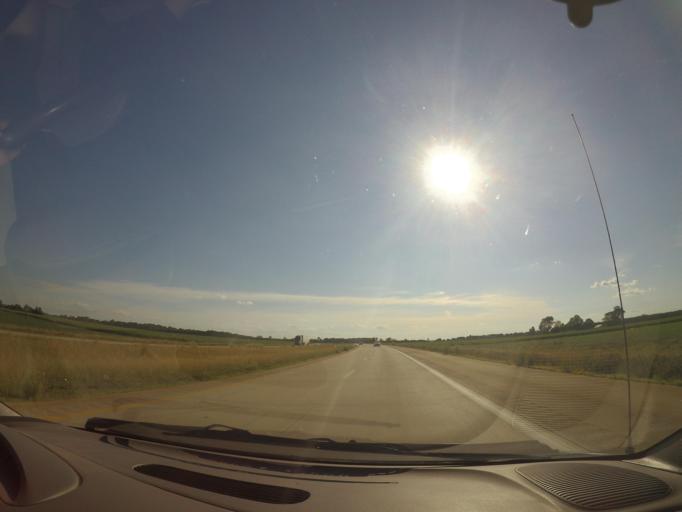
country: US
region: Ohio
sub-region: Lucas County
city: Whitehouse
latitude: 41.4334
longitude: -83.8776
